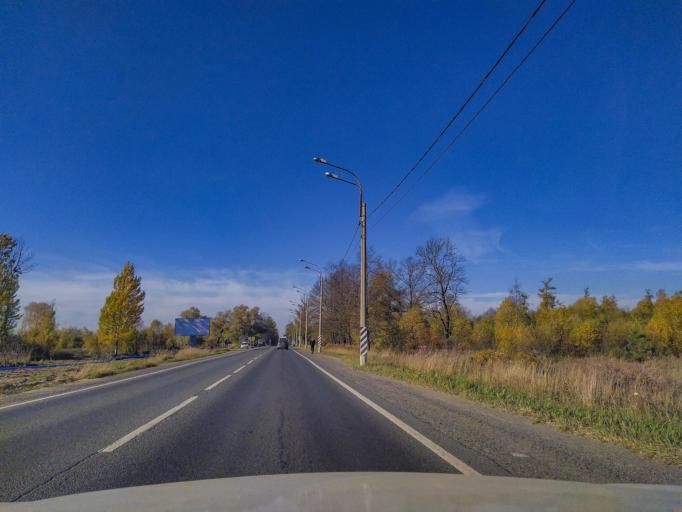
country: RU
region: St.-Petersburg
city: Aleksandrovskaya
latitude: 59.7041
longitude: 30.3472
